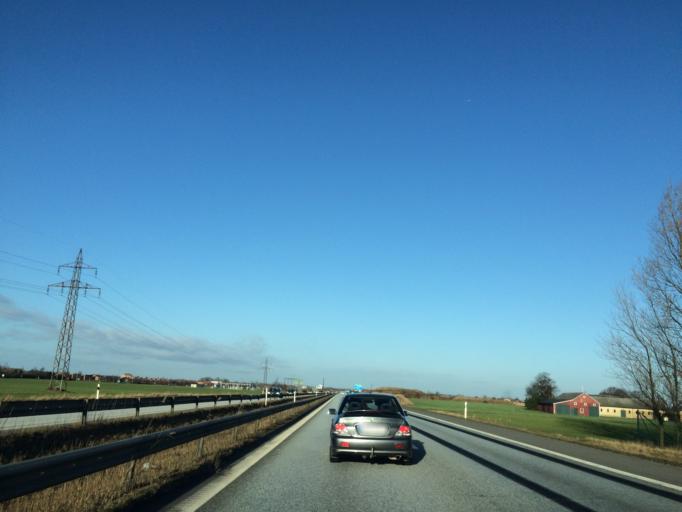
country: SE
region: Skane
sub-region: Lomma Kommun
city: Lomma
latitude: 55.6695
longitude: 13.0997
